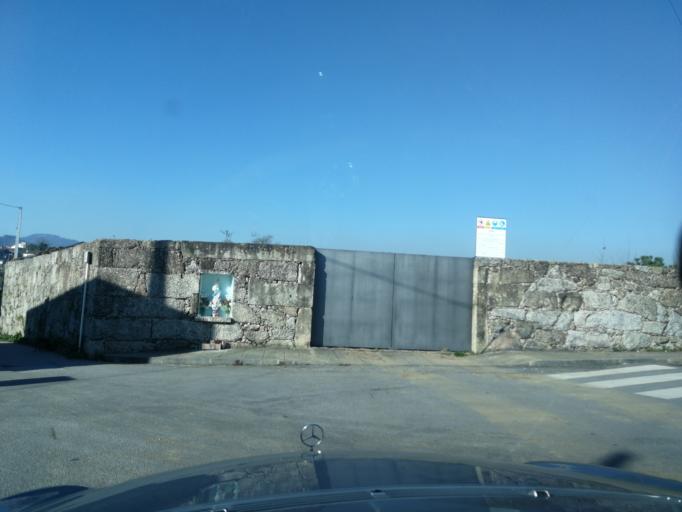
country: PT
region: Braga
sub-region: Guimaraes
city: Ponte
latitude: 41.4896
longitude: -8.3419
